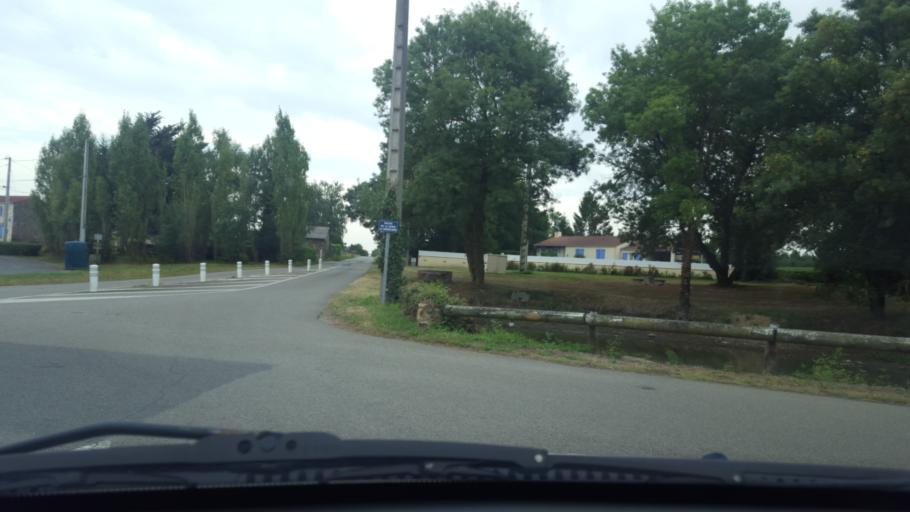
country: FR
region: Pays de la Loire
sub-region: Departement de la Loire-Atlantique
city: Saint-Philbert-de-Grand-Lieu
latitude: 47.0070
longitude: -1.6325
